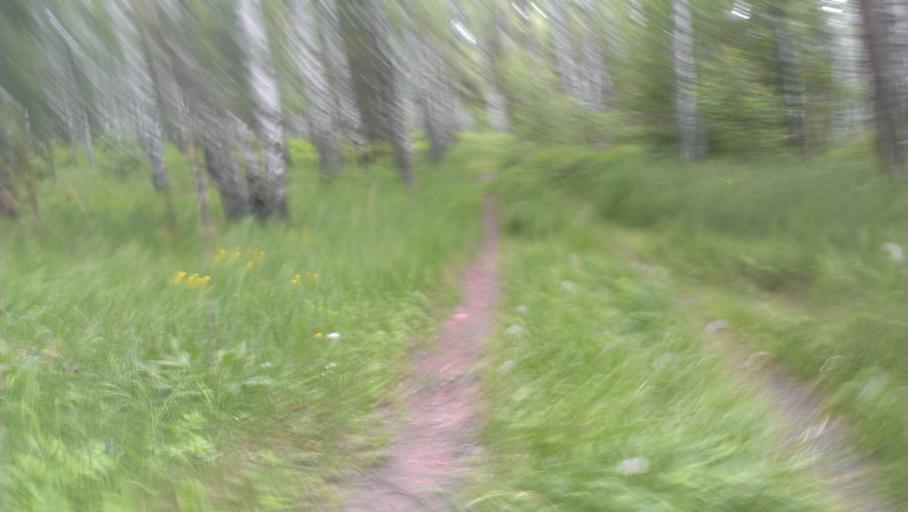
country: RU
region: Altai Krai
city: Sannikovo
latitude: 53.3402
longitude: 84.0484
